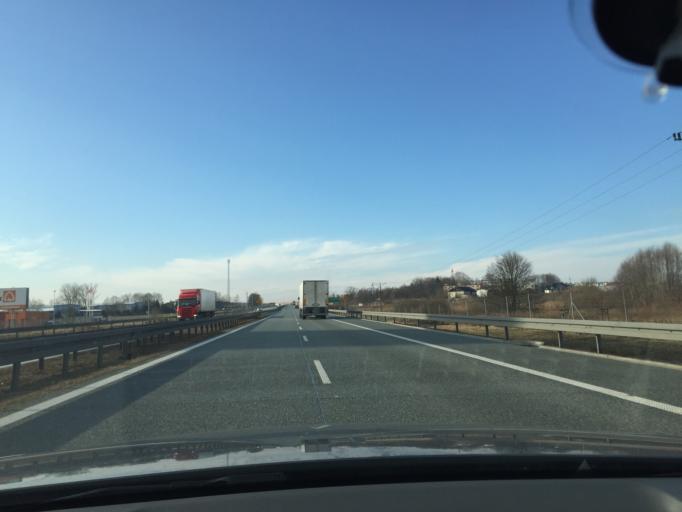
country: PL
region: Lodz Voivodeship
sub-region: Powiat rawski
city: Rawa Mazowiecka
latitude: 51.7632
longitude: 20.2669
